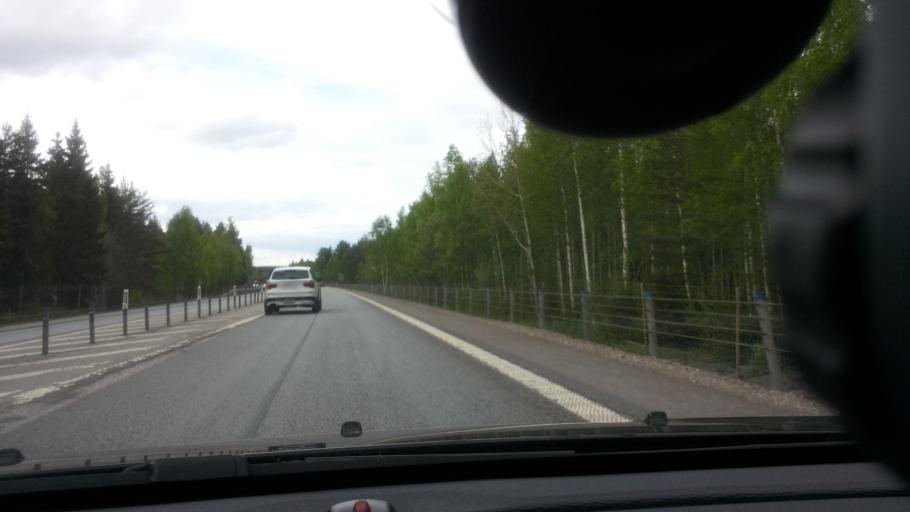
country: SE
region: Gaevleborg
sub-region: Gavle Kommun
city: Norrsundet
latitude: 60.9178
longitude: 17.0137
